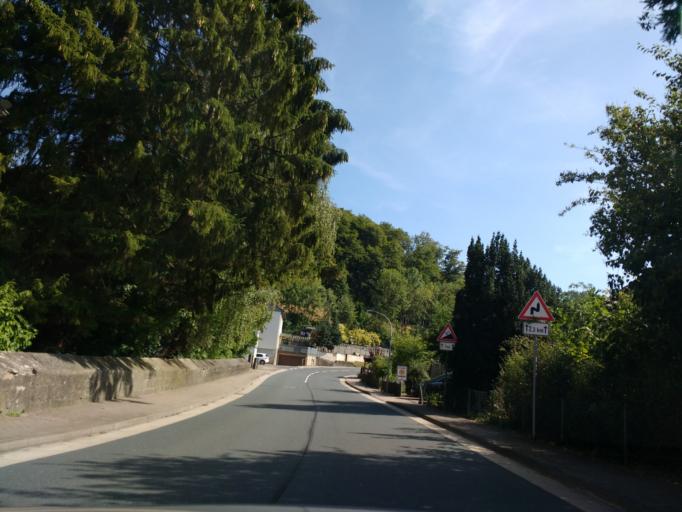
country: DE
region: Lower Saxony
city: Salzhemmendorf
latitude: 52.0757
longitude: 9.5533
